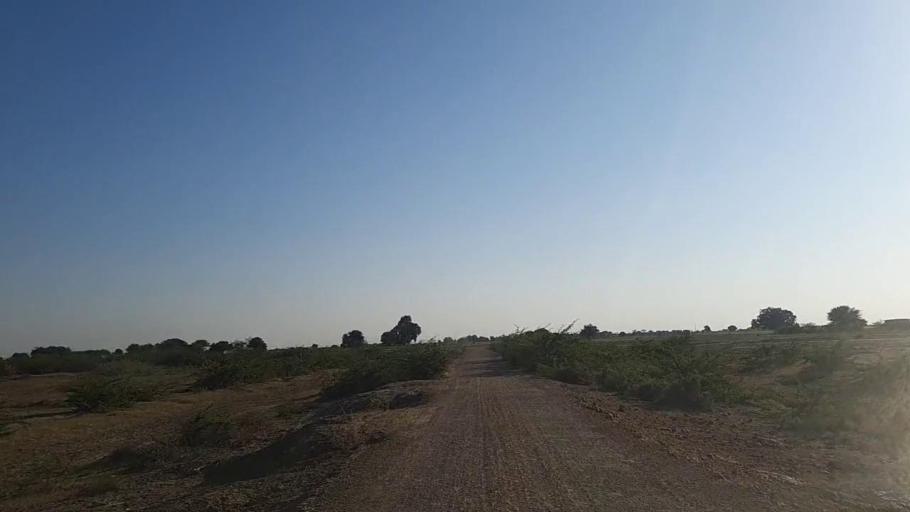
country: PK
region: Sindh
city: Naukot
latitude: 24.9525
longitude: 69.3876
